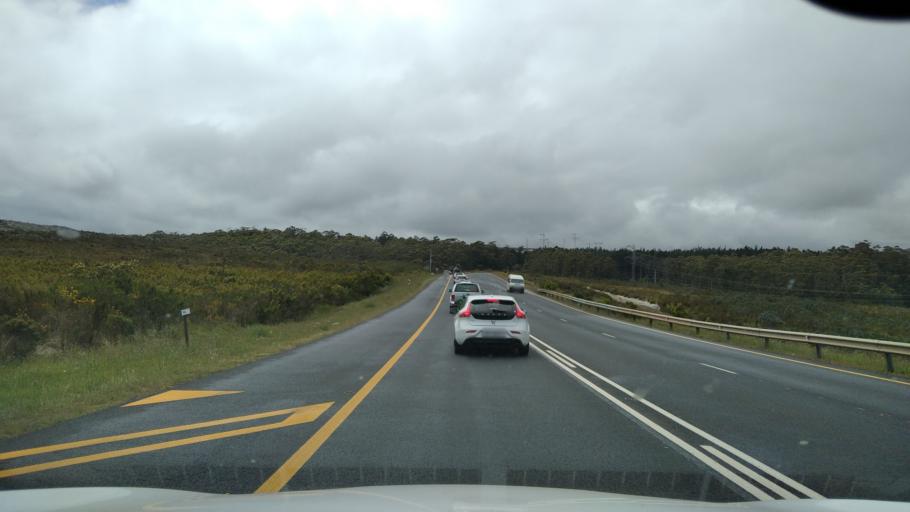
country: ZA
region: Western Cape
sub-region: Overberg District Municipality
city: Grabouw
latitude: -34.1518
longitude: 18.9361
